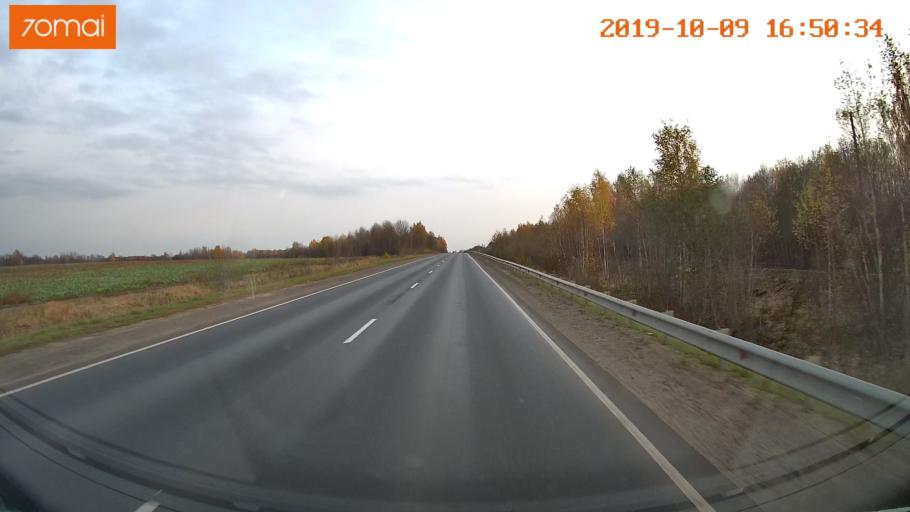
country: RU
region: Kostroma
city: Volgorechensk
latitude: 57.3992
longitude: 41.2105
